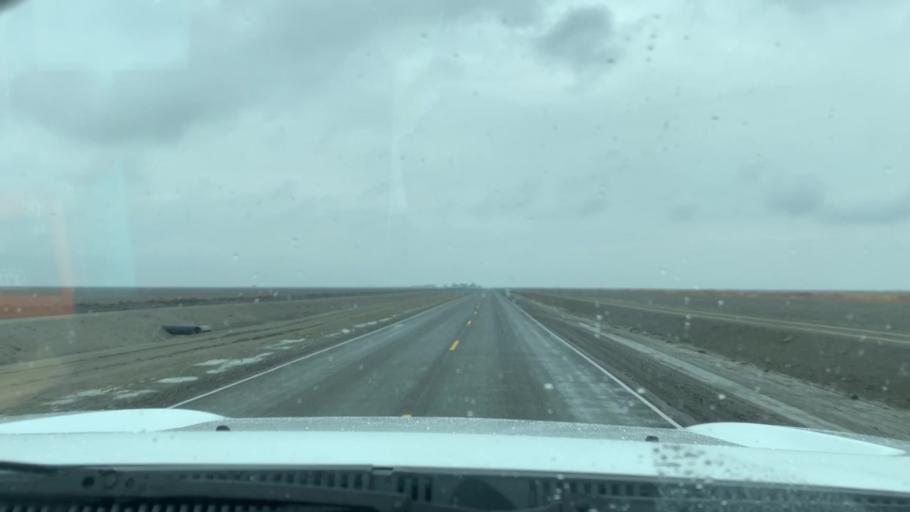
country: US
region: California
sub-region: Tulare County
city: Alpaugh
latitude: 35.9343
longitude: -119.6175
